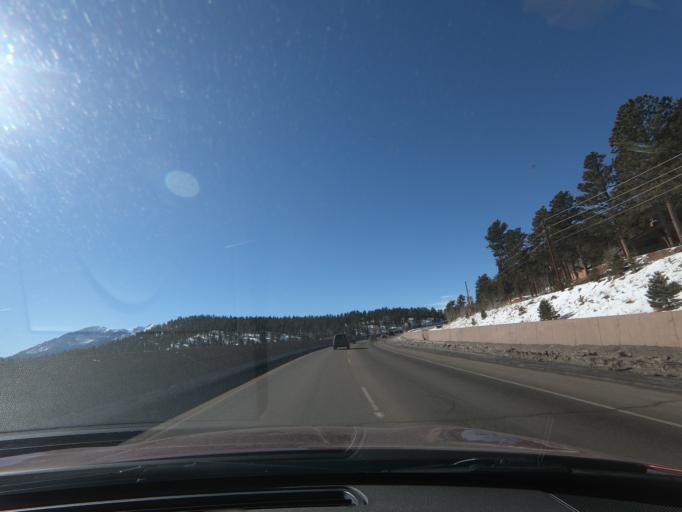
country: US
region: Colorado
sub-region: Teller County
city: Woodland Park
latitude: 38.9853
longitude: -105.0625
